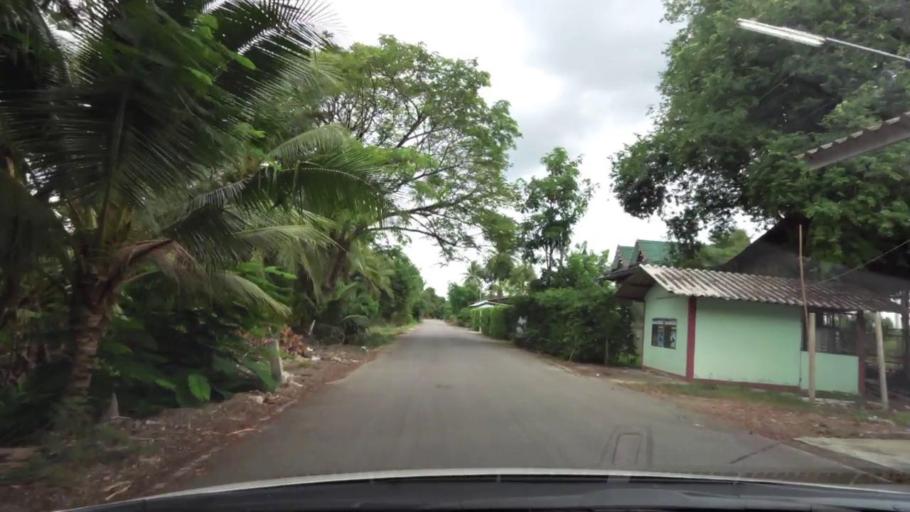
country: TH
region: Ratchaburi
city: Damnoen Saduak
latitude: 13.5543
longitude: 99.9909
